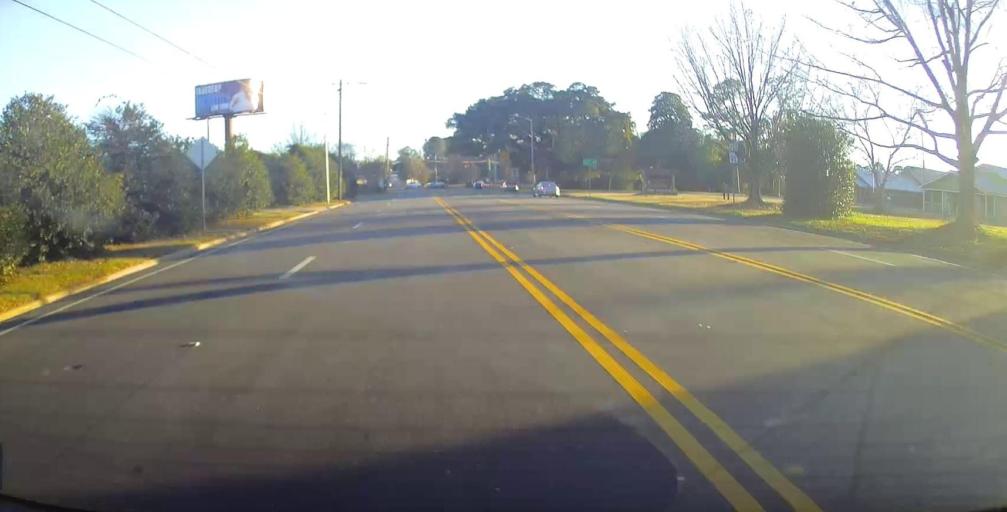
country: US
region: Georgia
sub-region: Dougherty County
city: Albany
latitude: 31.5481
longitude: -84.1767
